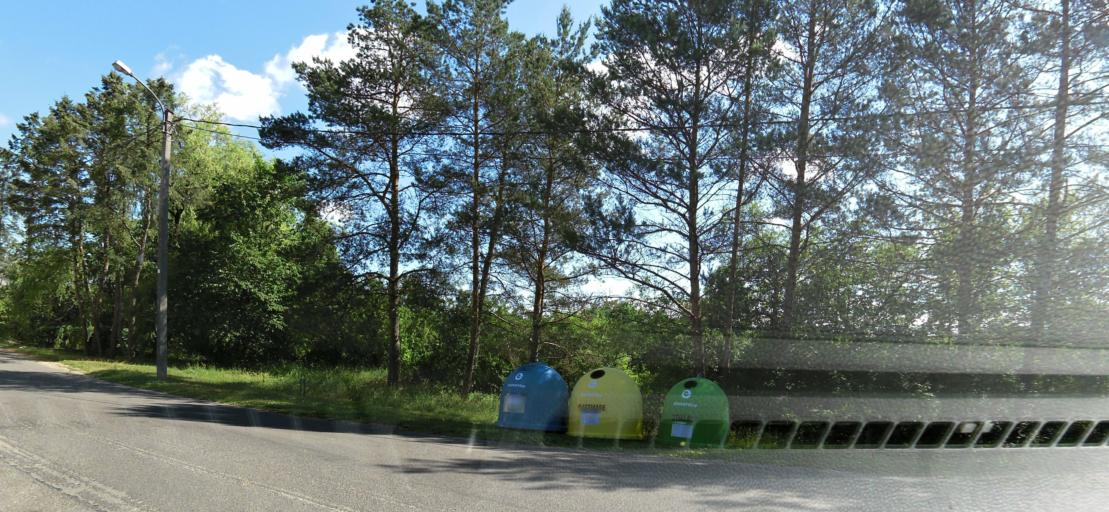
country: LT
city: Nemencine
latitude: 54.7945
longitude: 25.3975
